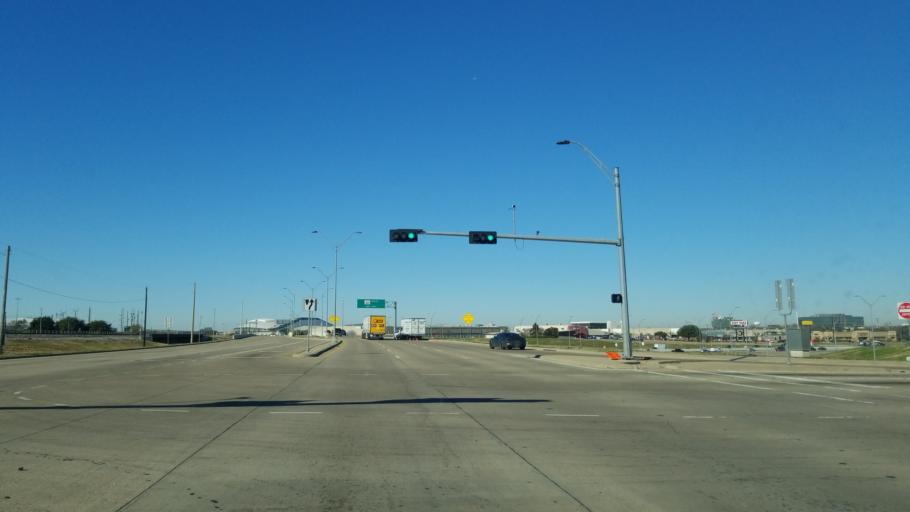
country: US
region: Texas
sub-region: Tarrant County
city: Arlington
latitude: 32.7419
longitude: -97.0586
